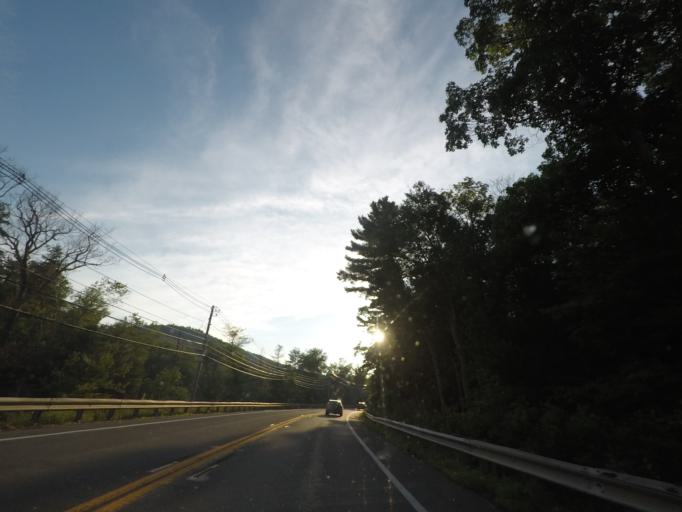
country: US
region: Massachusetts
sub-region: Hampden County
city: Brimfield
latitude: 42.1140
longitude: -72.2289
